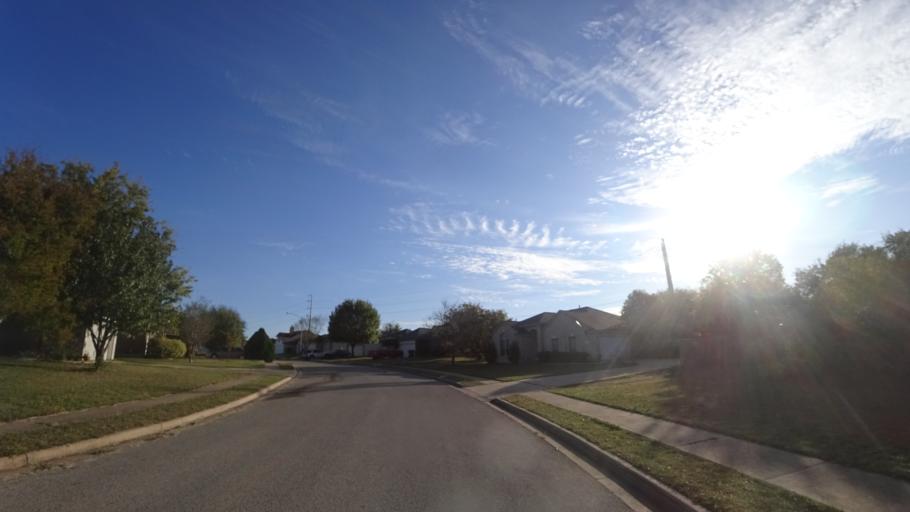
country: US
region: Texas
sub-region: Travis County
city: Wells Branch
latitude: 30.4175
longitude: -97.6558
